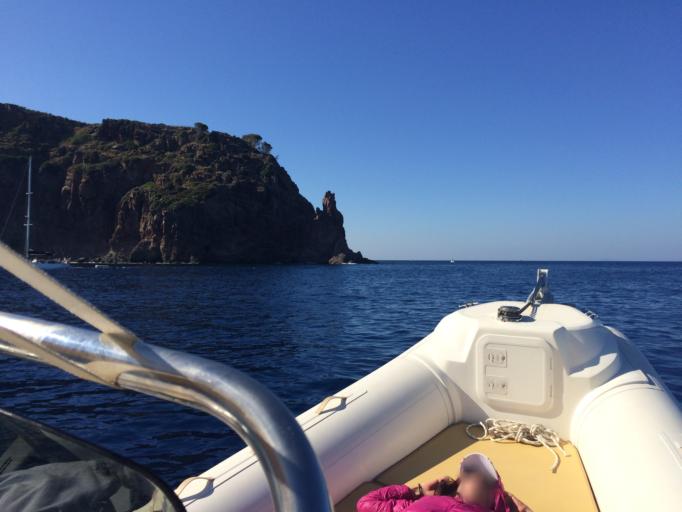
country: IT
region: Tuscany
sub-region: Provincia di Livorno
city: Capraia Isola
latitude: 43.0422
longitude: 9.8492
